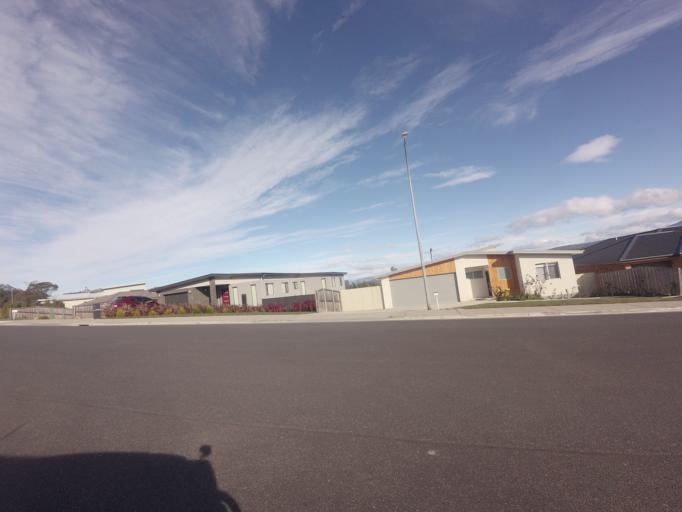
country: AU
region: Tasmania
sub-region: Clarence
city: Rokeby
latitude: -42.9037
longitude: 147.4565
